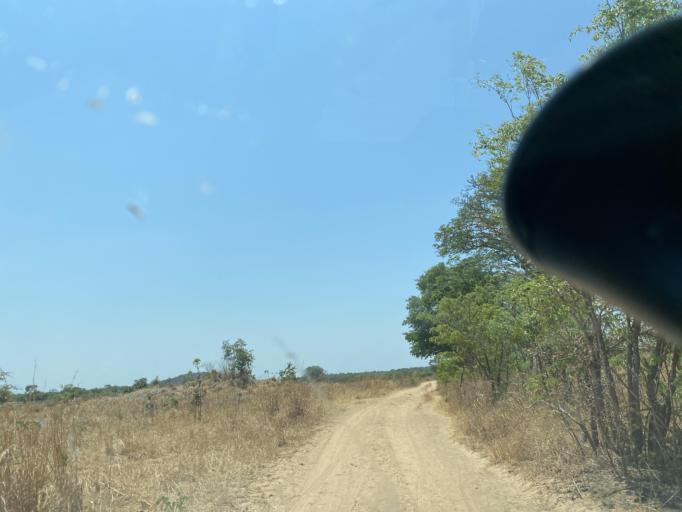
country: ZM
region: Lusaka
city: Chongwe
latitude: -15.4323
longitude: 29.1922
